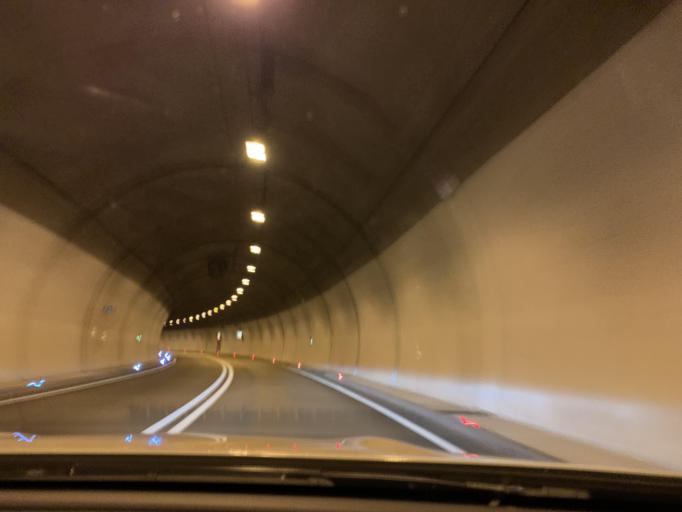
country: IT
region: Trentino-Alto Adige
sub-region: Bolzano
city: Cornedo All'Isarco
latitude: 46.4756
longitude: 11.4055
